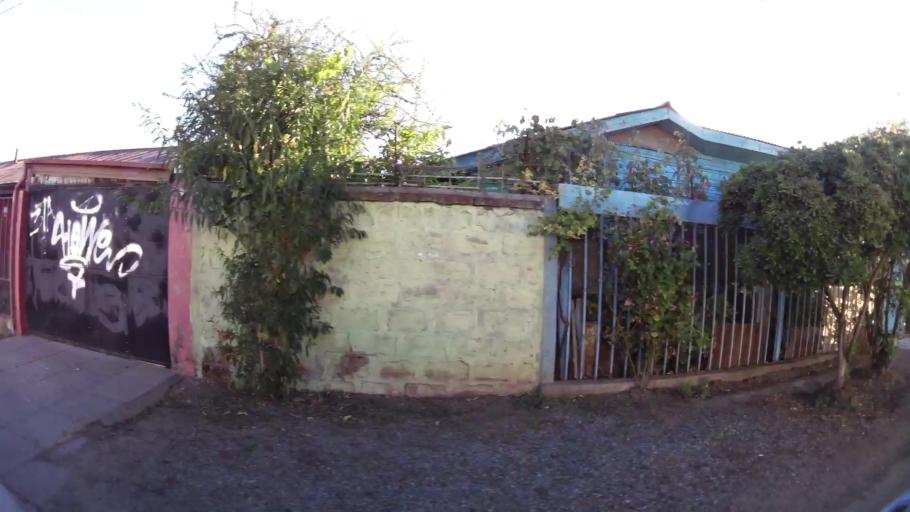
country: CL
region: O'Higgins
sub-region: Provincia de Cachapoal
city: Rancagua
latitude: -34.1696
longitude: -70.7186
